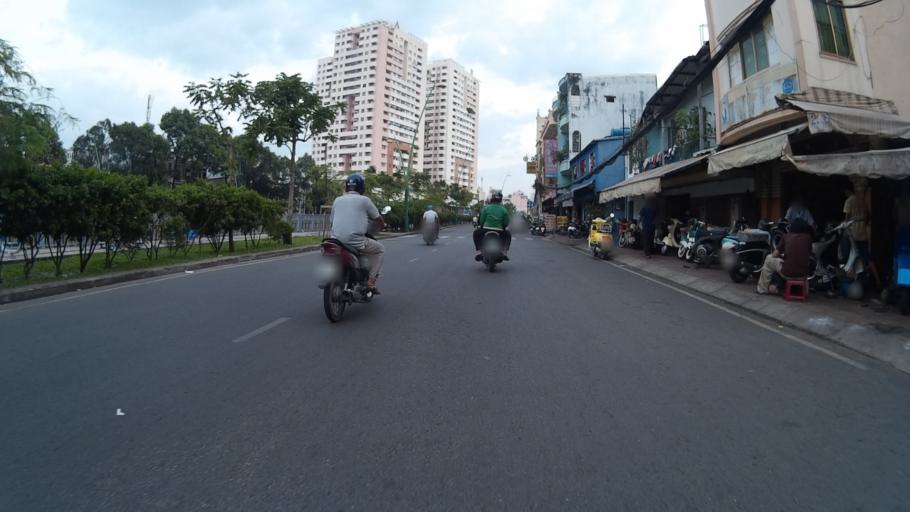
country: VN
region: Ho Chi Minh City
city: Quan Phu Nhuan
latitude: 10.7867
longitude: 106.6733
